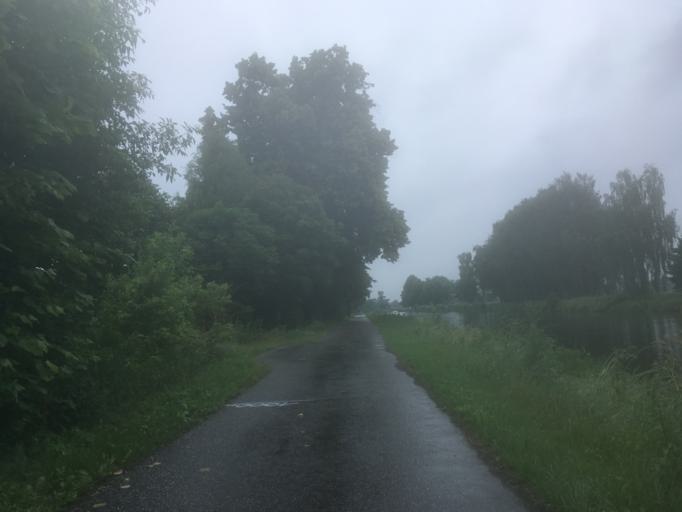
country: DE
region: Brandenburg
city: Zehdenick
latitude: 52.9363
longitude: 13.3774
